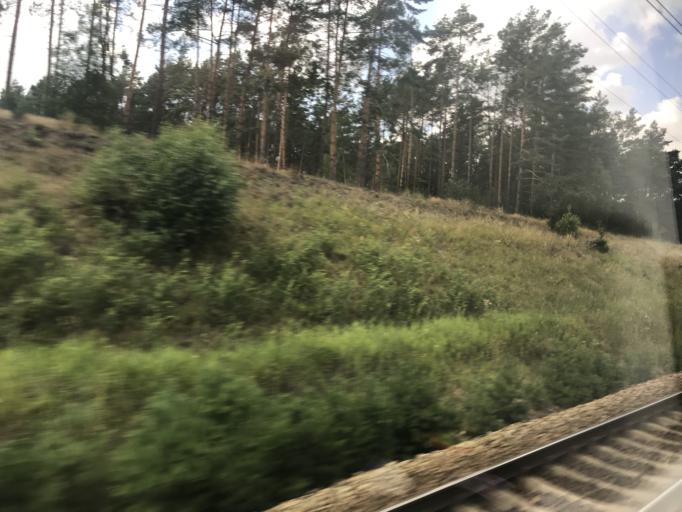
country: PL
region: Lubusz
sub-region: Powiat sulecinski
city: Torzym
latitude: 52.3019
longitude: 15.0782
